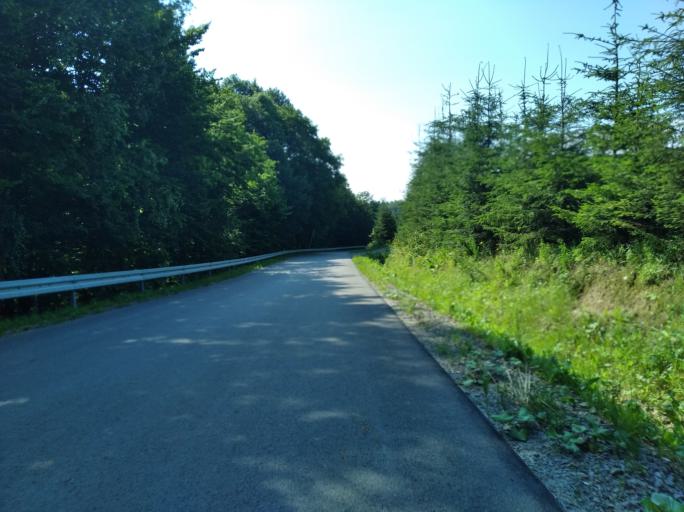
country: PL
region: Subcarpathian Voivodeship
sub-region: Powiat brzozowski
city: Wesola
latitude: 49.8328
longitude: 22.1457
